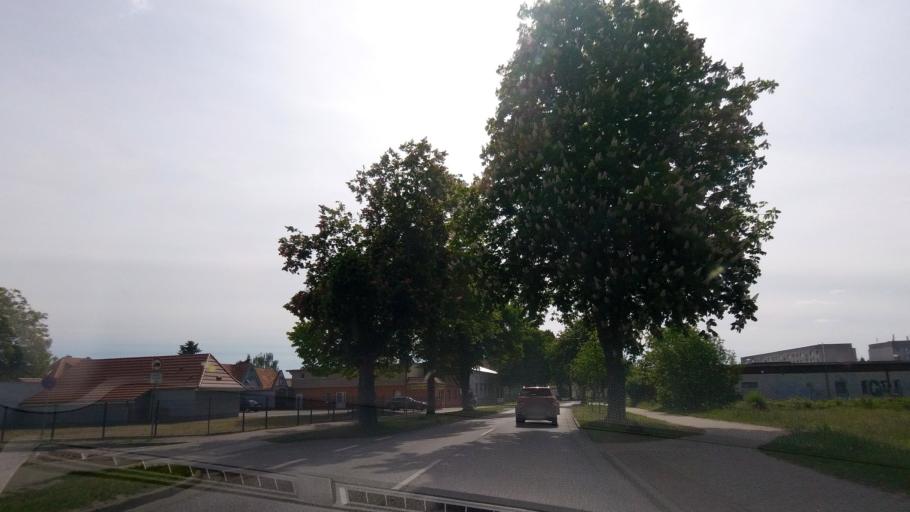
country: DE
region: Brandenburg
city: Wittstock
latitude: 53.1572
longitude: 12.4812
